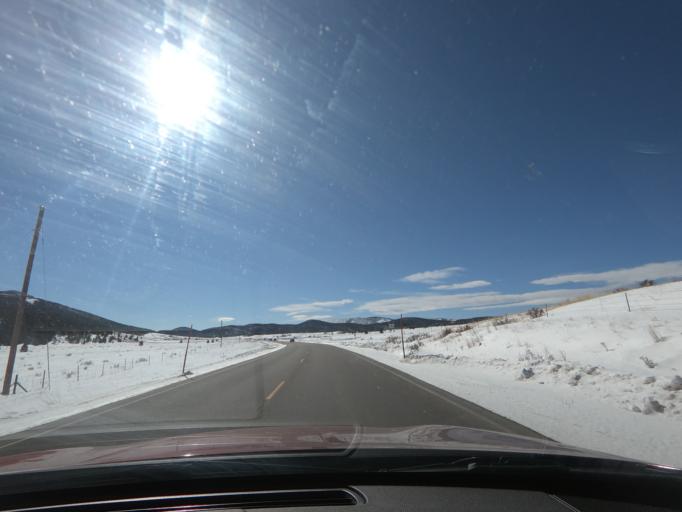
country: US
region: Colorado
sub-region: Teller County
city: Cripple Creek
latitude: 38.7915
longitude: -105.1245
